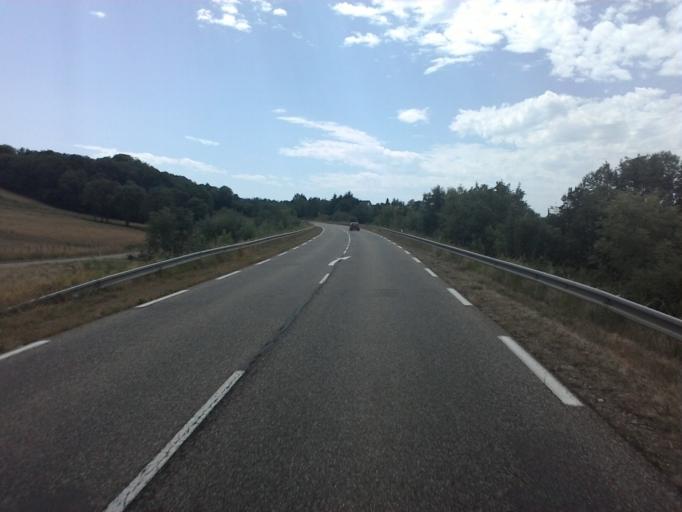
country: FR
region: Franche-Comte
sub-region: Departement du Jura
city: Saint-Amour
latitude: 46.4461
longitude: 5.3470
